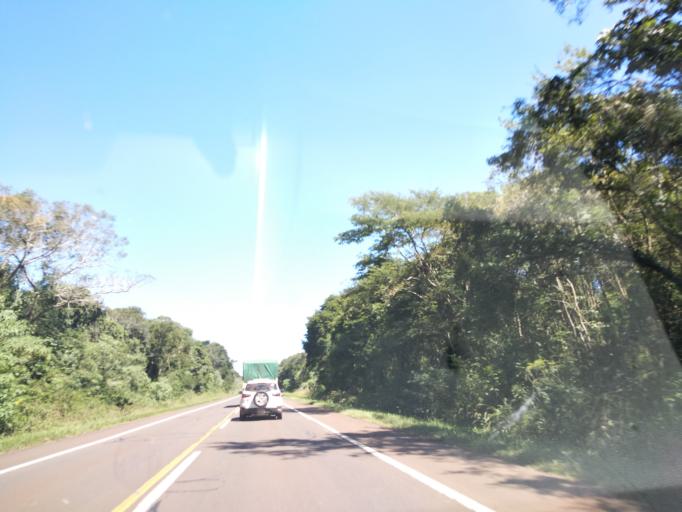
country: AR
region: Misiones
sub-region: Departamento de Iguazu
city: Puerto Iguazu
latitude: -25.7095
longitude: -54.5172
